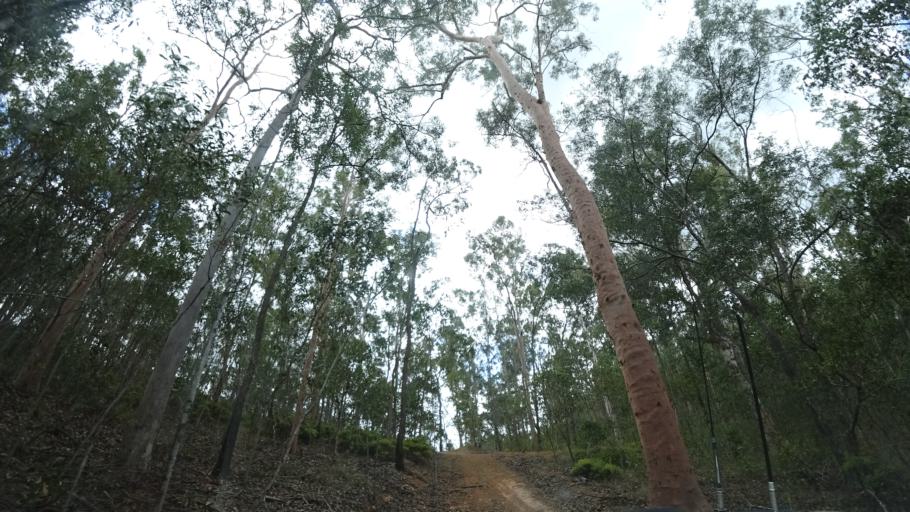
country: AU
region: Queensland
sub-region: Moreton Bay
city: Highvale
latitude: -27.4241
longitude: 152.7406
